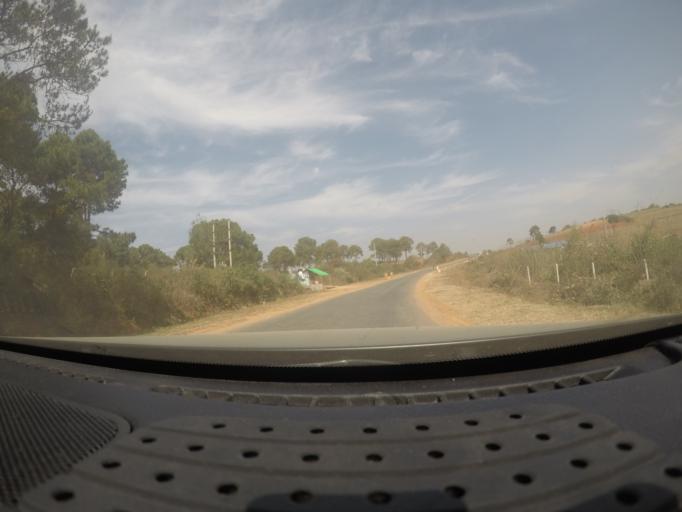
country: MM
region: Shan
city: Taunggyi
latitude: 20.6972
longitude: 96.6268
